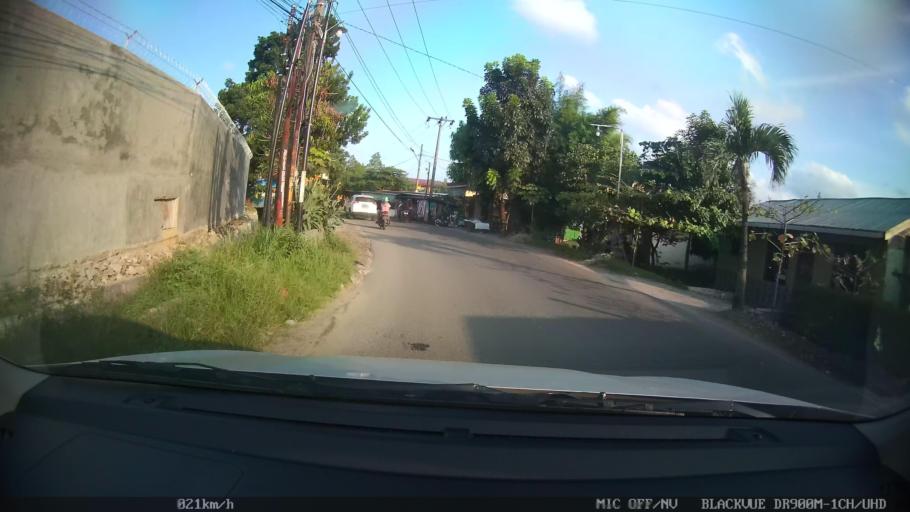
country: ID
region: North Sumatra
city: Medan
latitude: 3.6244
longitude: 98.6636
